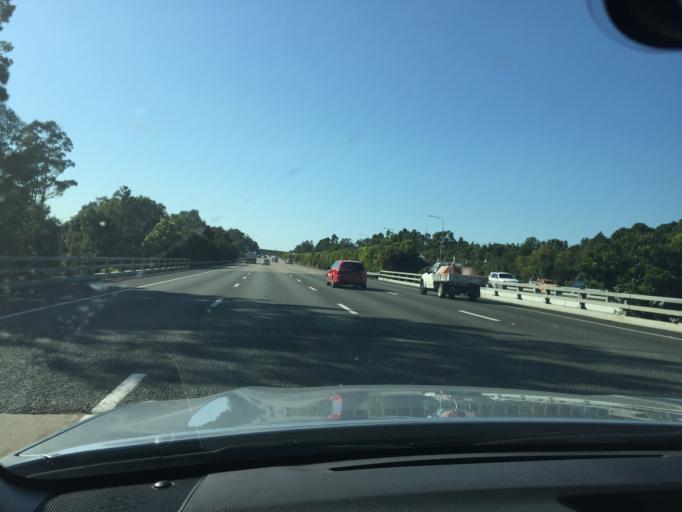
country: AU
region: Queensland
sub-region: Gold Coast
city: Ormeau Hills
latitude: -27.8165
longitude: 153.2810
